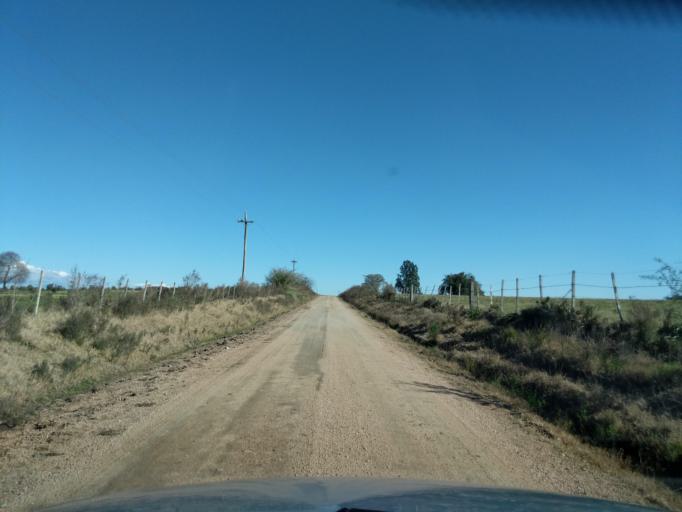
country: UY
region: Florida
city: Florida
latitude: -34.0804
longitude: -56.2608
